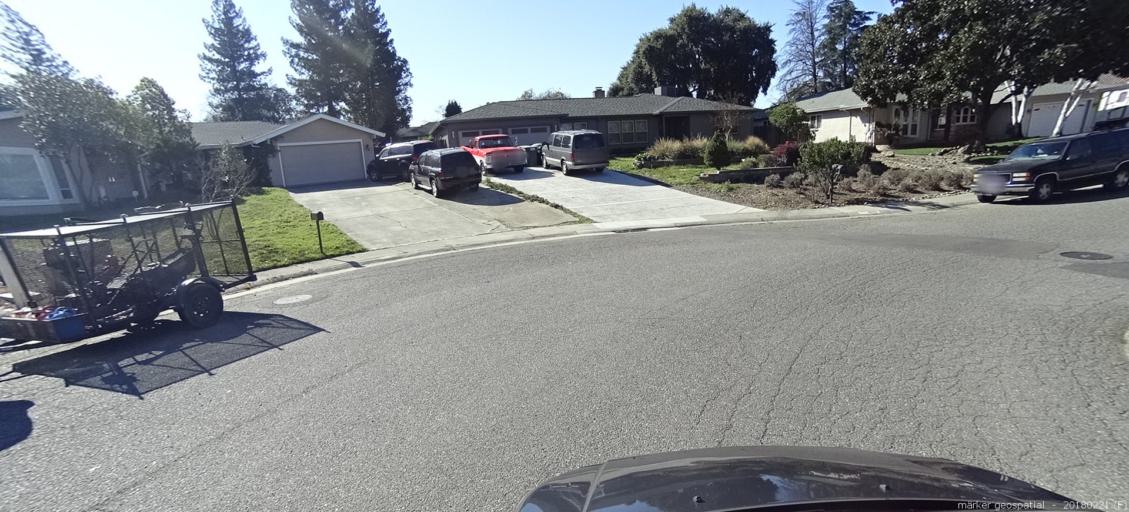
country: US
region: California
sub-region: Sacramento County
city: Orangevale
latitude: 38.6820
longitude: -121.2380
